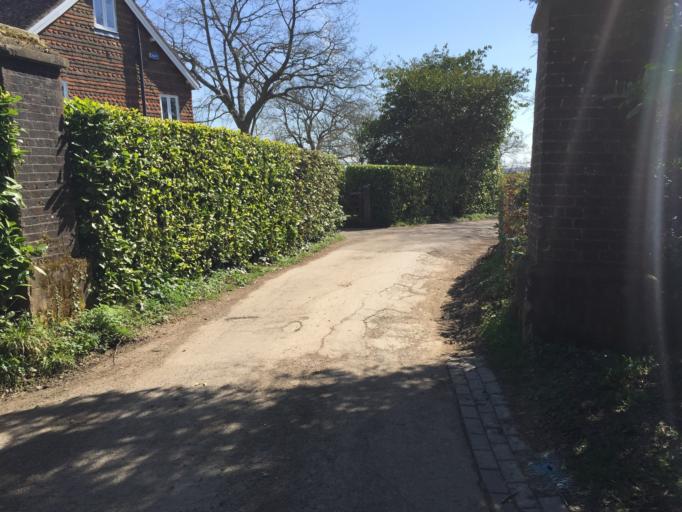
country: GB
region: England
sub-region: East Sussex
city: Wadhurst
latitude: 51.0322
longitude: 0.2858
